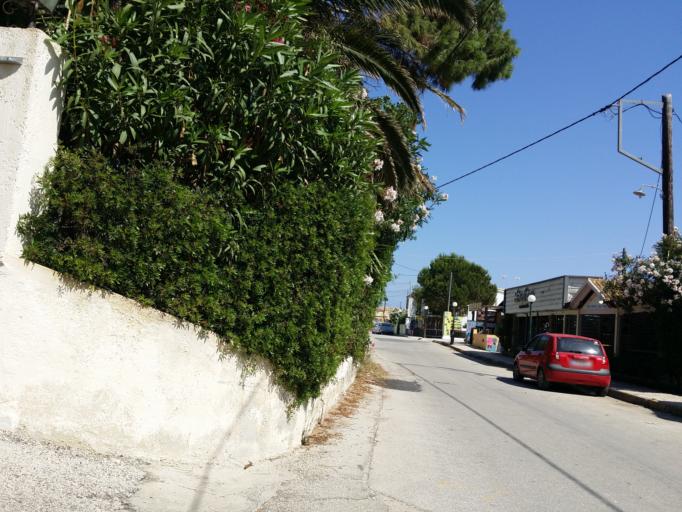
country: GR
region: Ionian Islands
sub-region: Nomos Kerkyras
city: Perivoli
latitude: 39.4281
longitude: 19.9420
